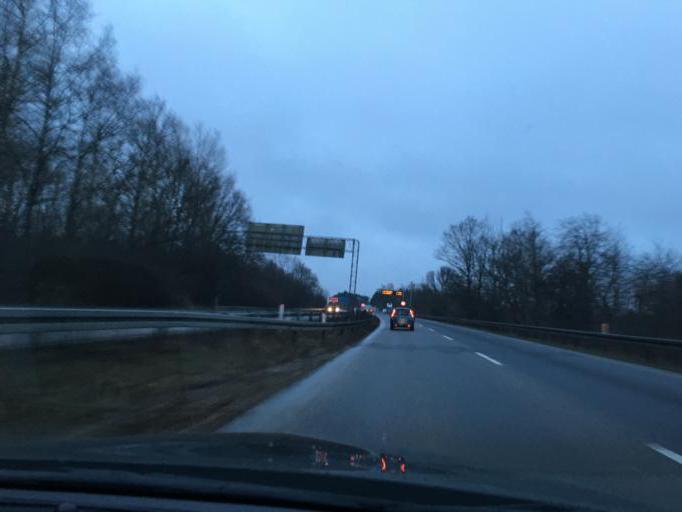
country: DK
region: Capital Region
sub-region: Horsholm Kommune
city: Horsholm
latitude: 55.8688
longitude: 12.4830
